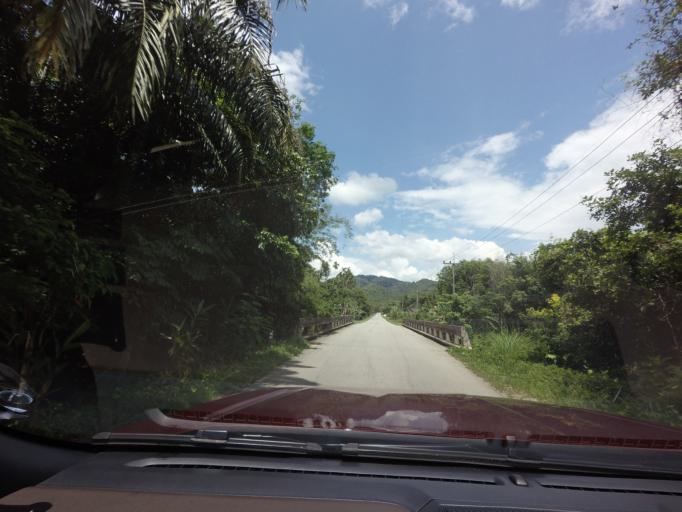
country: TH
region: Narathiwat
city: Chanae
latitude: 6.0915
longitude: 101.6910
